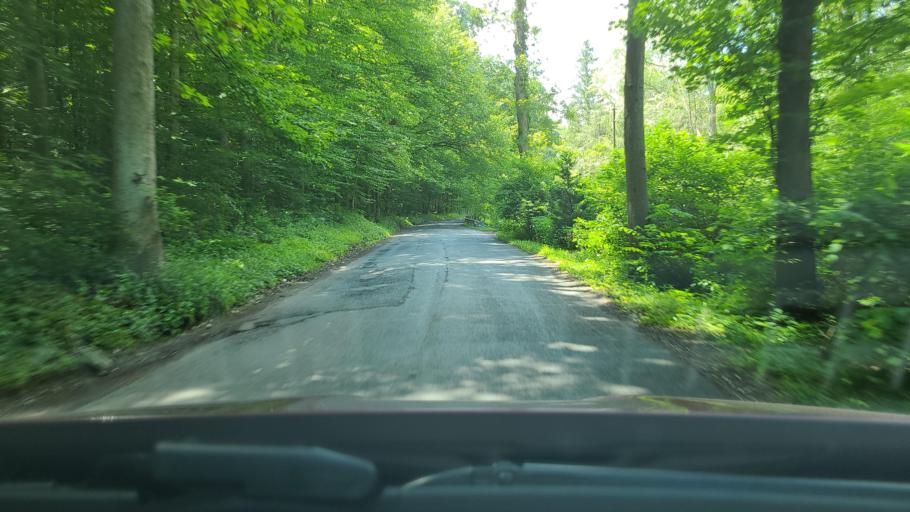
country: US
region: Maryland
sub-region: Montgomery County
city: Damascus
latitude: 39.2686
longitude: -77.2426
